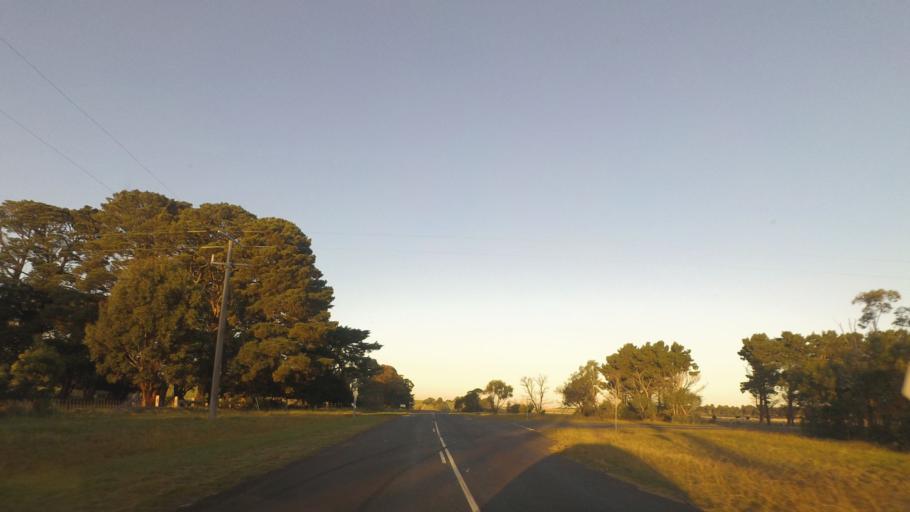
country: AU
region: Victoria
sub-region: Hume
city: Sunbury
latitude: -37.5210
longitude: 144.6352
